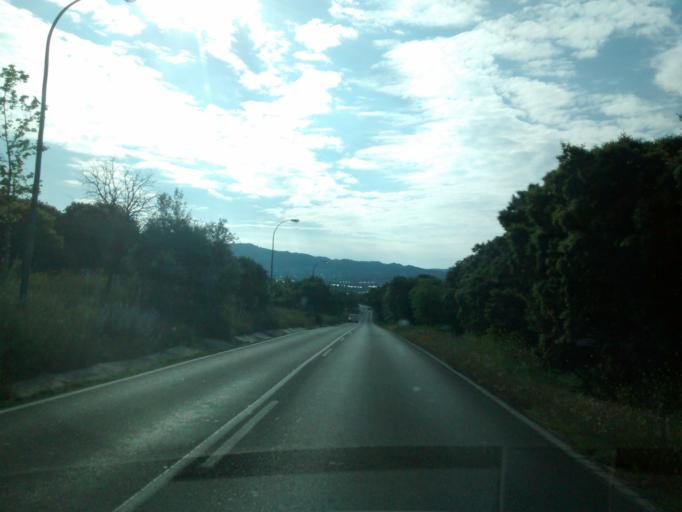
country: ES
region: Madrid
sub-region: Provincia de Madrid
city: Alpedrete
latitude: 40.6529
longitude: -4.0178
